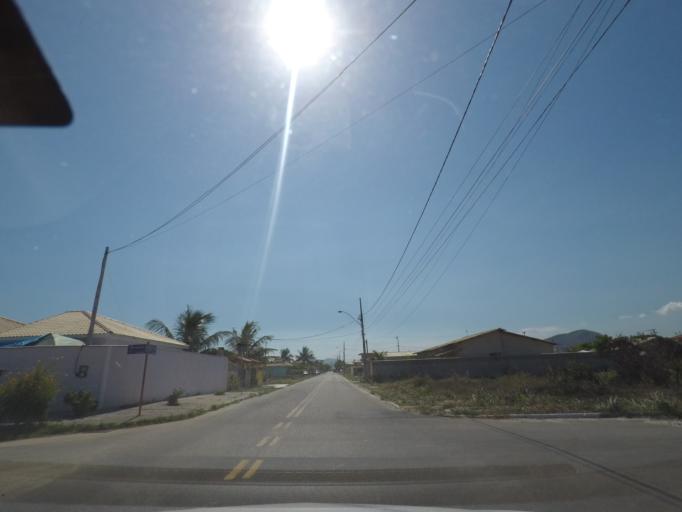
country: BR
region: Rio de Janeiro
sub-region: Marica
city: Marica
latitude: -22.9670
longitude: -42.9172
